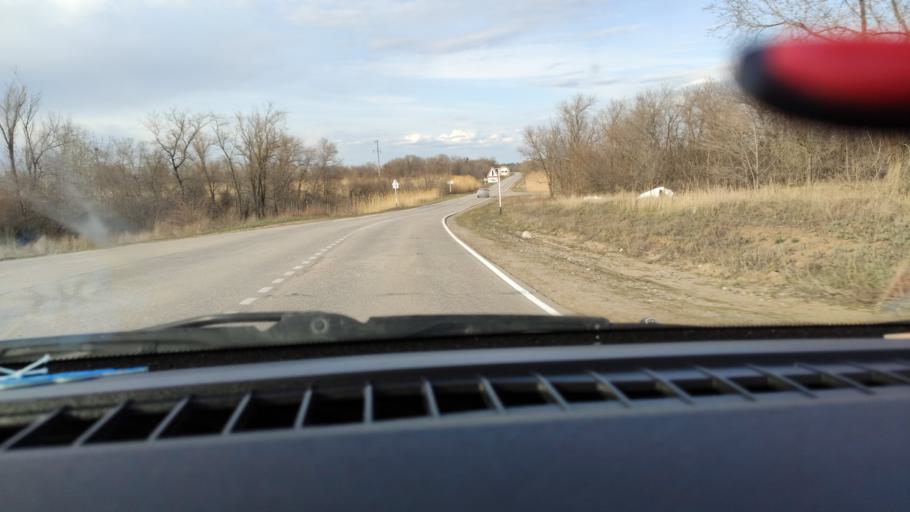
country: RU
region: Saratov
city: Privolzhskiy
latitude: 51.2393
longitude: 45.9275
